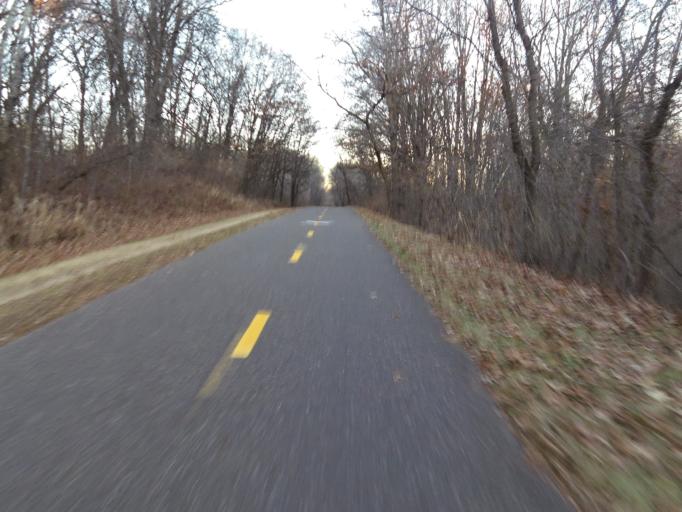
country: US
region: Minnesota
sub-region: Washington County
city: Grant
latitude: 45.0808
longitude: -92.8960
